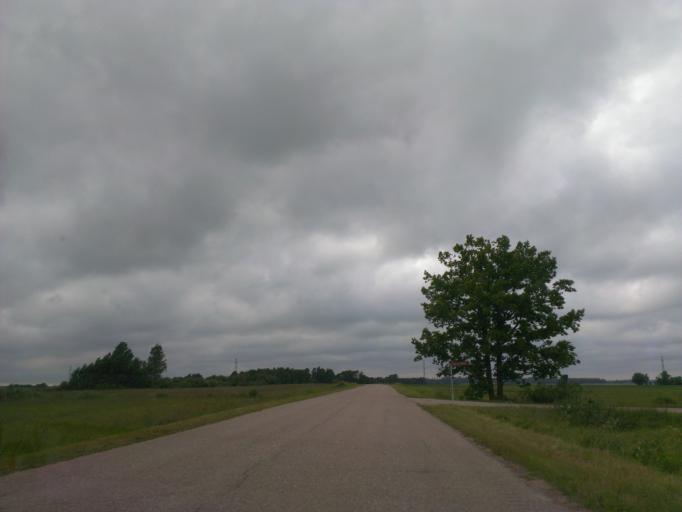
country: LV
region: Aizpute
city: Aizpute
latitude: 56.7193
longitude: 21.4478
